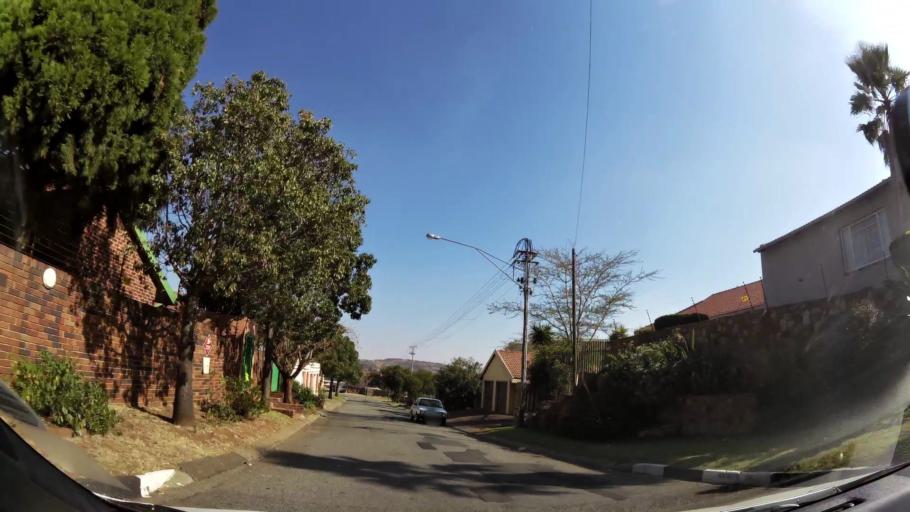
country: ZA
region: Gauteng
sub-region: City of Johannesburg Metropolitan Municipality
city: Johannesburg
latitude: -26.2677
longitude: 28.0449
